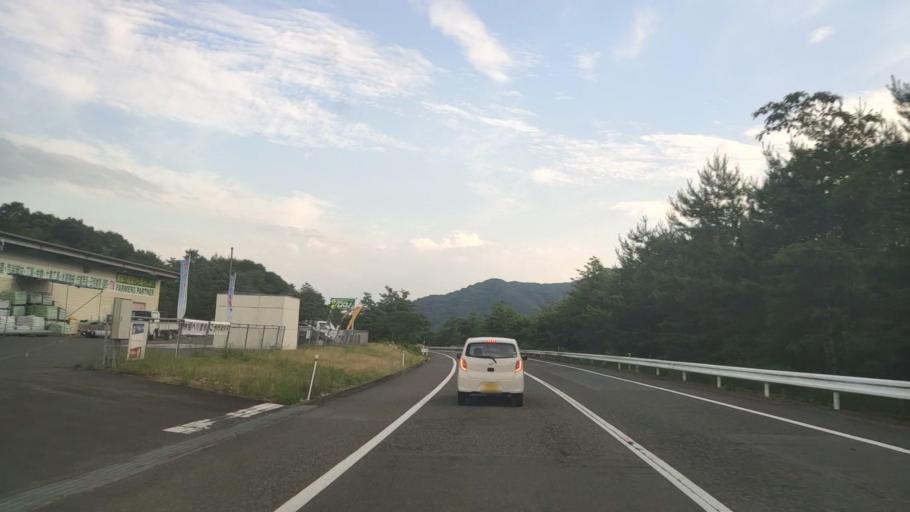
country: JP
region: Tottori
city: Kurayoshi
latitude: 35.2979
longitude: 133.7364
